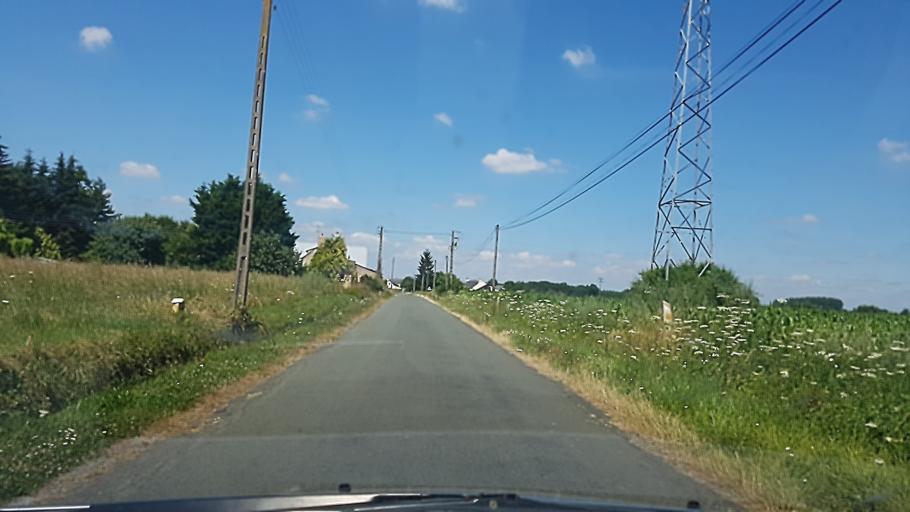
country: FR
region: Pays de la Loire
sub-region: Departement de Maine-et-Loire
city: Corze
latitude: 47.5436
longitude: -0.3872
